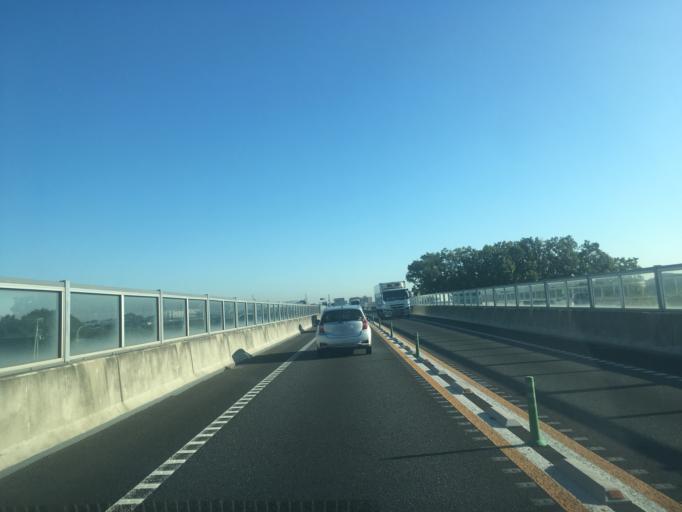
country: JP
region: Saitama
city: Kukichuo
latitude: 36.0557
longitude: 139.6924
